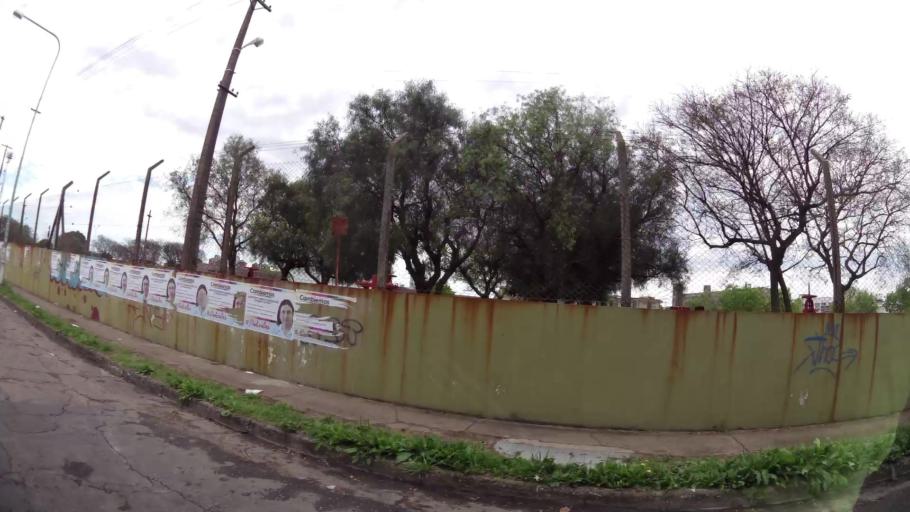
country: AR
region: Buenos Aires
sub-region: Partido de Quilmes
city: Quilmes
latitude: -34.7525
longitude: -58.2225
